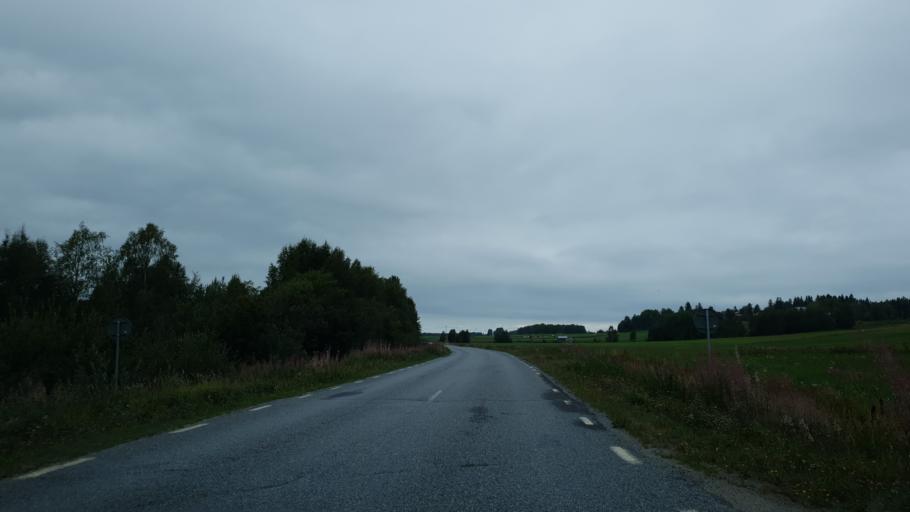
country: SE
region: Vaesterbotten
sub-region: Skelleftea Kommun
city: Burea
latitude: 64.4050
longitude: 21.2854
